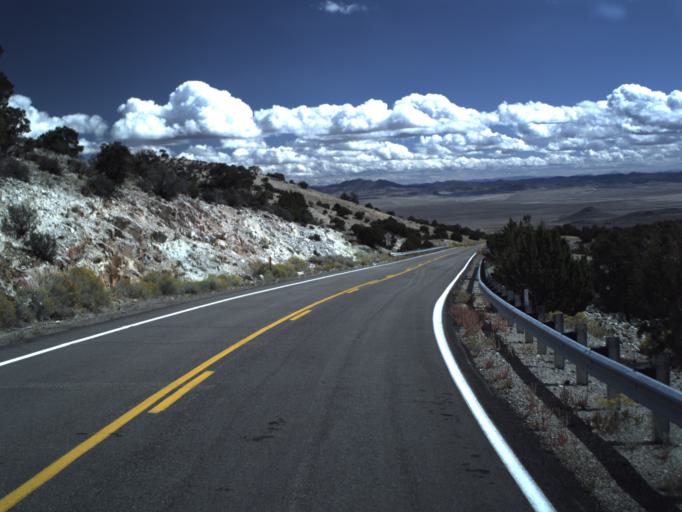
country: US
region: Utah
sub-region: Beaver County
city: Milford
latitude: 38.5176
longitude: -113.5387
